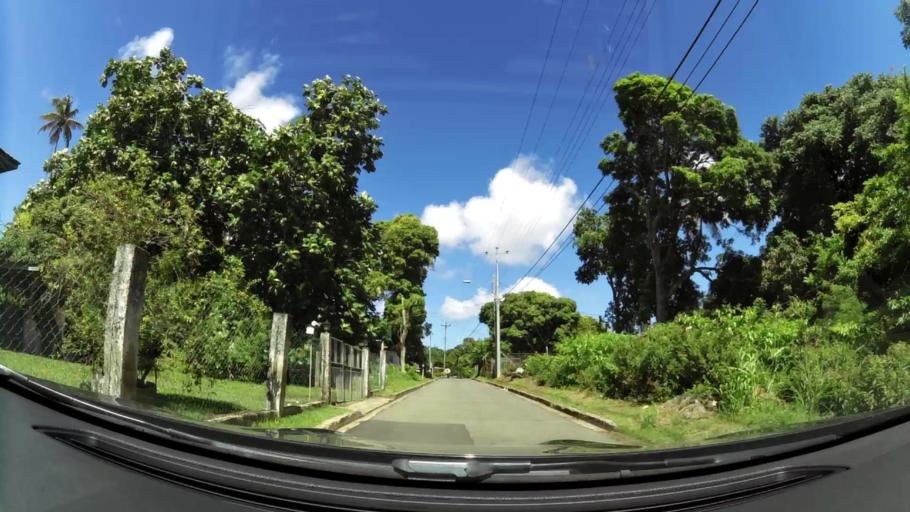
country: TT
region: Tobago
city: Scarborough
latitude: 11.1689
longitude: -60.7835
